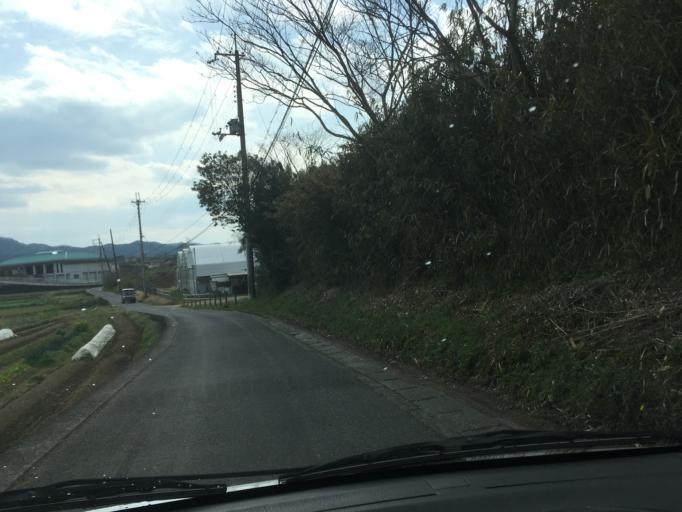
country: JP
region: Nara
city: Kashihara-shi
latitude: 34.4536
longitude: 135.7916
